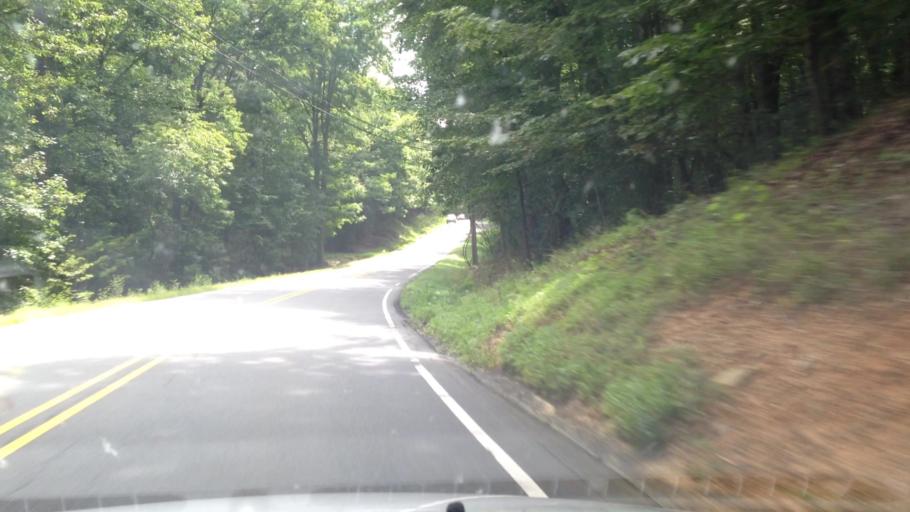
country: US
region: North Carolina
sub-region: Rockingham County
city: Wentworth
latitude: 36.3972
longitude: -79.8018
